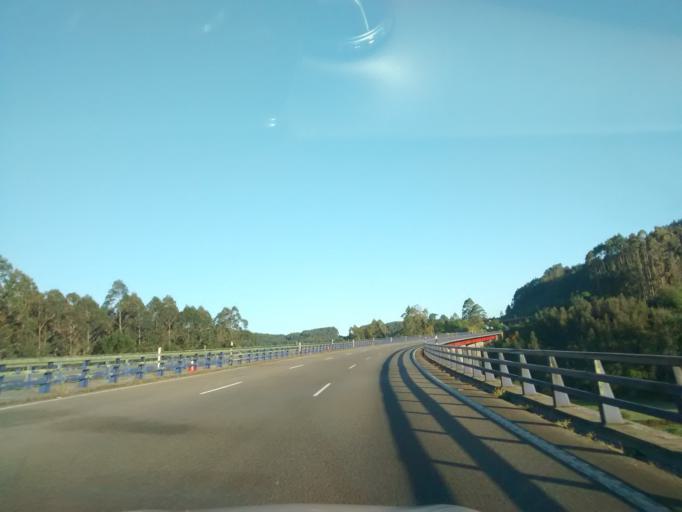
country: ES
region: Asturias
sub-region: Province of Asturias
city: Colunga
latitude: 43.4883
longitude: -5.3164
